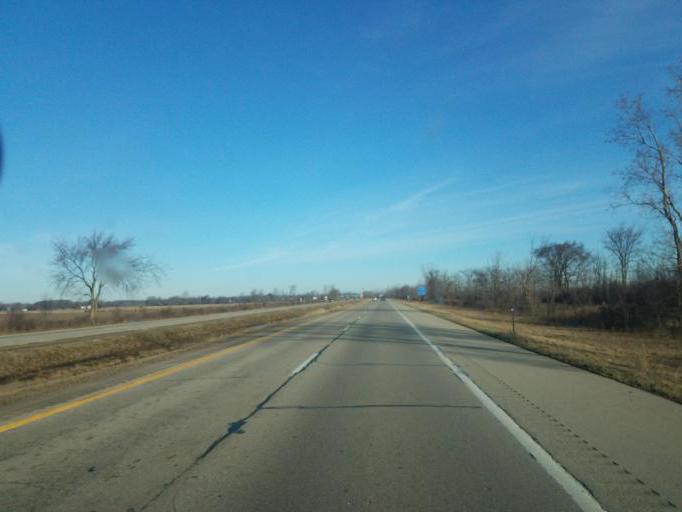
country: US
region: Michigan
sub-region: Gratiot County
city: Ithaca
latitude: 43.2737
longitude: -84.5684
